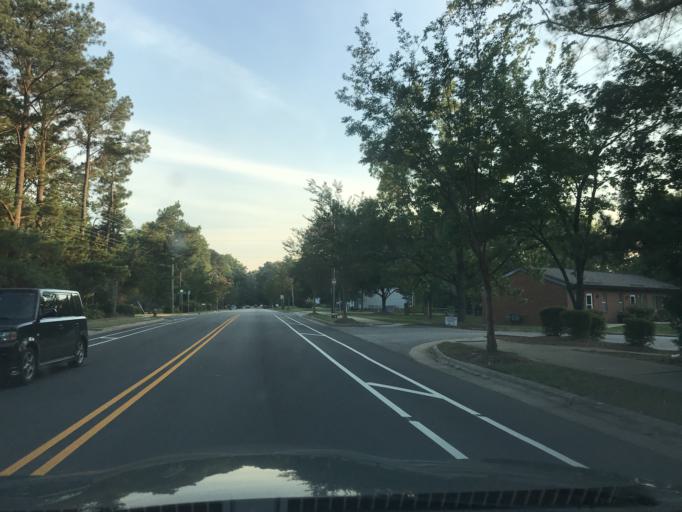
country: US
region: North Carolina
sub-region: Wake County
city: Raleigh
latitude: 35.7520
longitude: -78.6167
